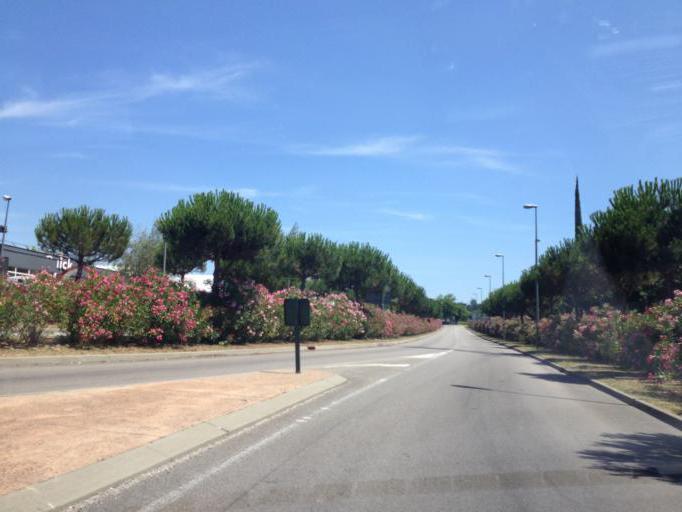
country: FR
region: Rhone-Alpes
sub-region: Departement de l'Ardeche
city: Guilherand-Granges
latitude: 44.9055
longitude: 4.8789
